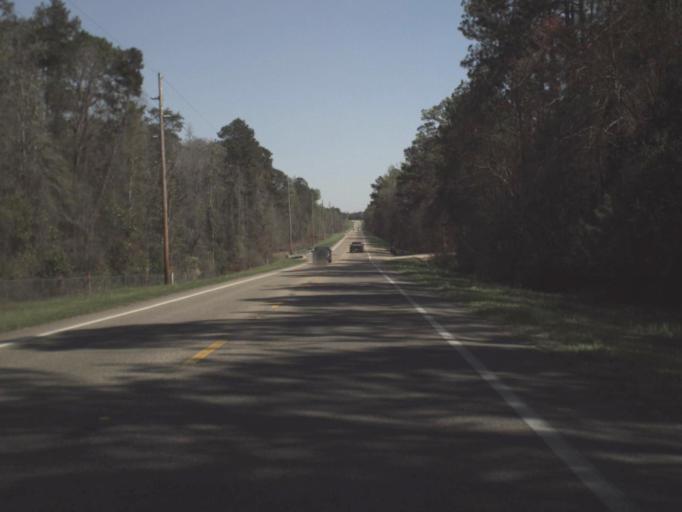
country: US
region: Florida
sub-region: Liberty County
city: Bristol
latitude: 30.4298
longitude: -84.9373
